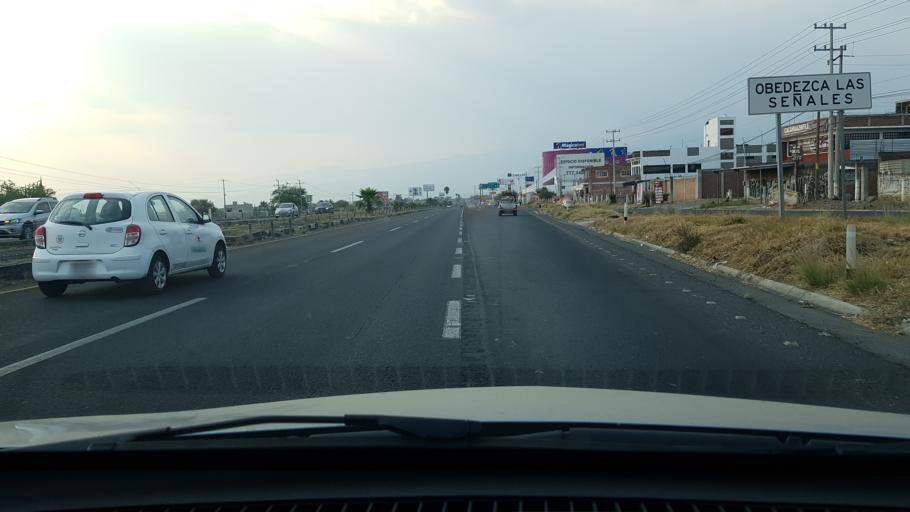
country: MX
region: Morelos
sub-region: Cuautla
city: Tierra Larga (Campo Nuevo)
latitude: 18.8632
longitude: -98.9479
